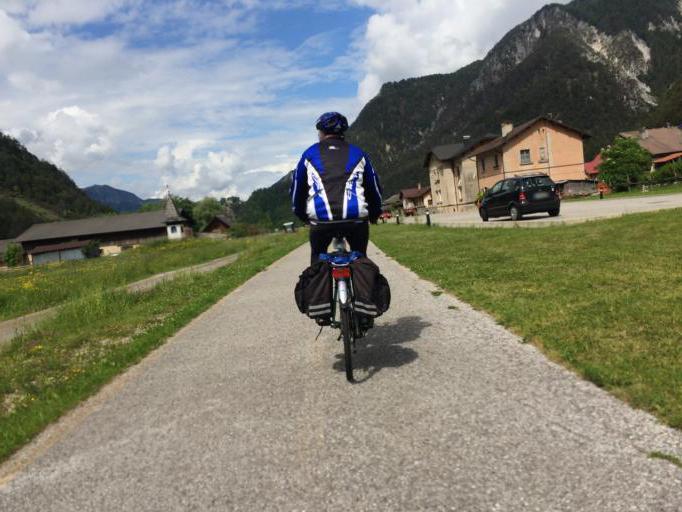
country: IT
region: Friuli Venezia Giulia
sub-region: Provincia di Udine
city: Malborghetto
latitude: 46.5096
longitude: 13.4737
